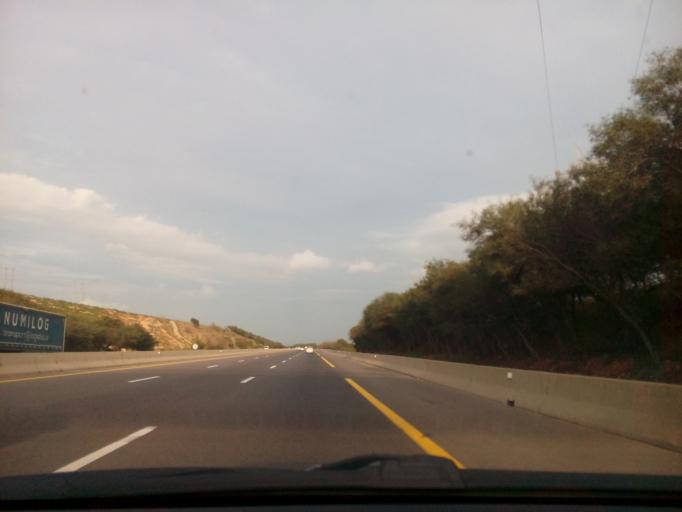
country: DZ
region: Relizane
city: Relizane
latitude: 35.7549
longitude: 0.3586
